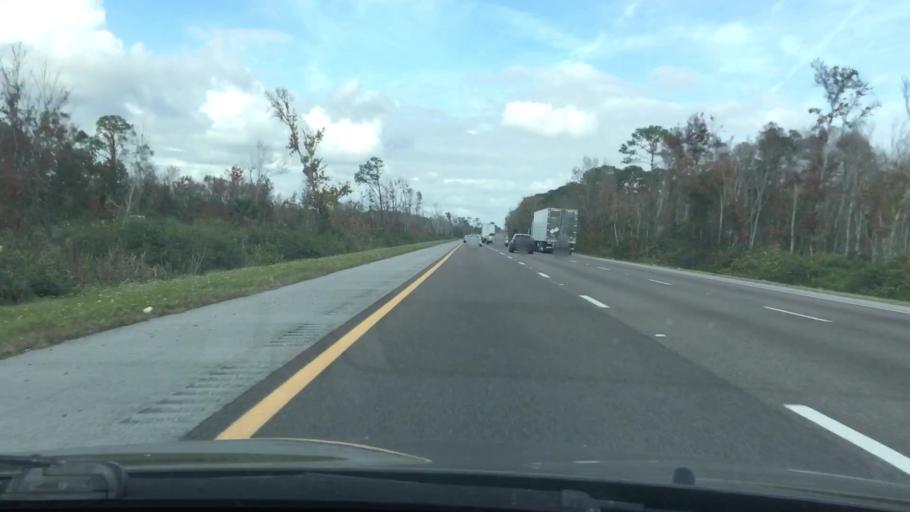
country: US
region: Florida
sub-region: Volusia County
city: Oak Hill
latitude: 28.8978
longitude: -80.9299
